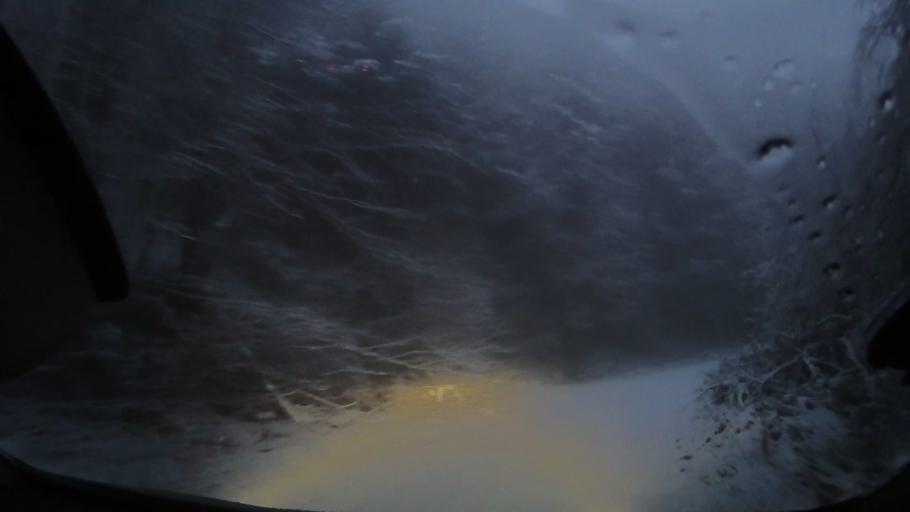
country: RO
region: Alba
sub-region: Comuna Avram Iancu
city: Avram Iancu
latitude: 46.3180
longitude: 22.8030
